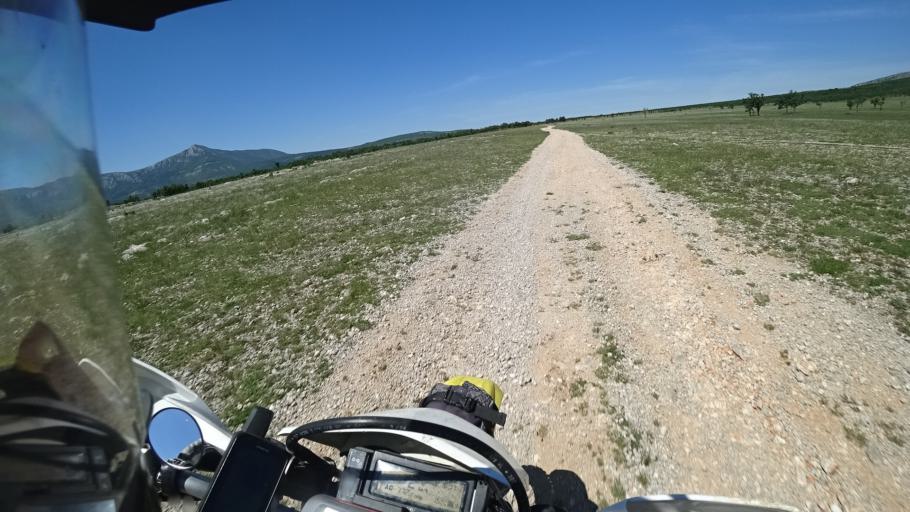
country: BA
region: Federation of Bosnia and Herzegovina
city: Bosansko Grahovo
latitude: 44.0043
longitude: 16.3962
